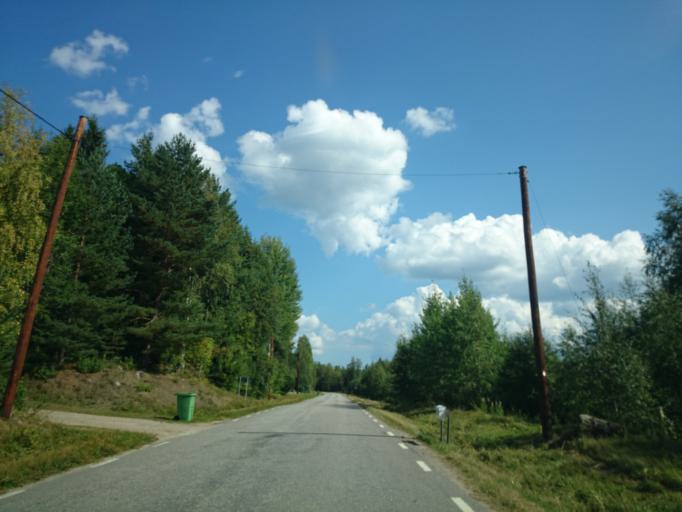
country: SE
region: Gaevleborg
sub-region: Ljusdals Kommun
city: Jaervsoe
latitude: 61.7929
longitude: 16.2117
